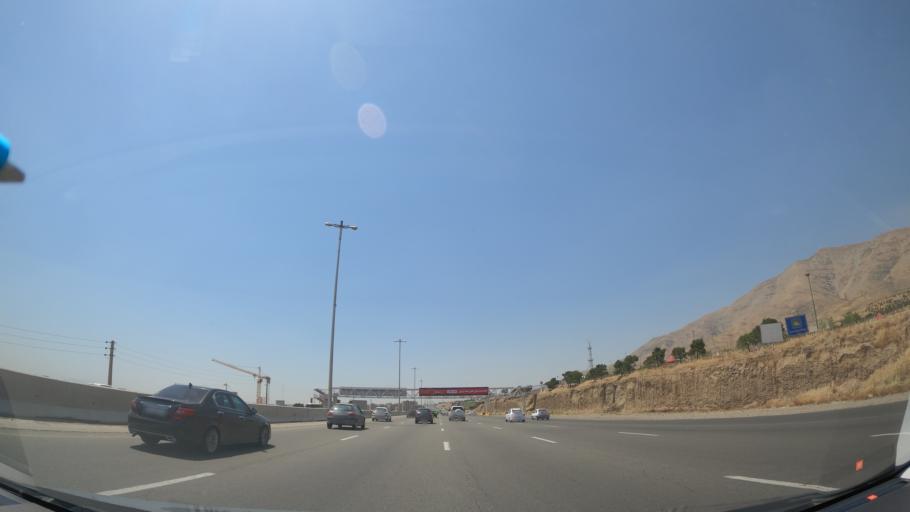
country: IR
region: Tehran
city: Shahr-e Qods
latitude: 35.7497
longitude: 51.0820
